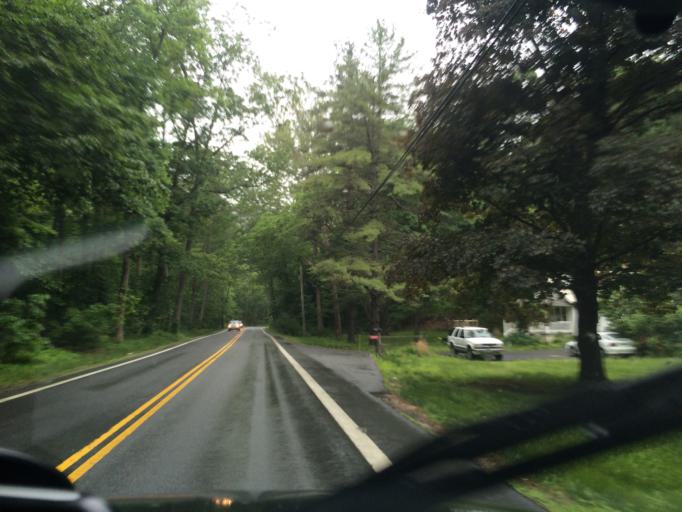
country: US
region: Maryland
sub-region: Frederick County
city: Thurmont
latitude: 39.6473
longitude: -77.4190
